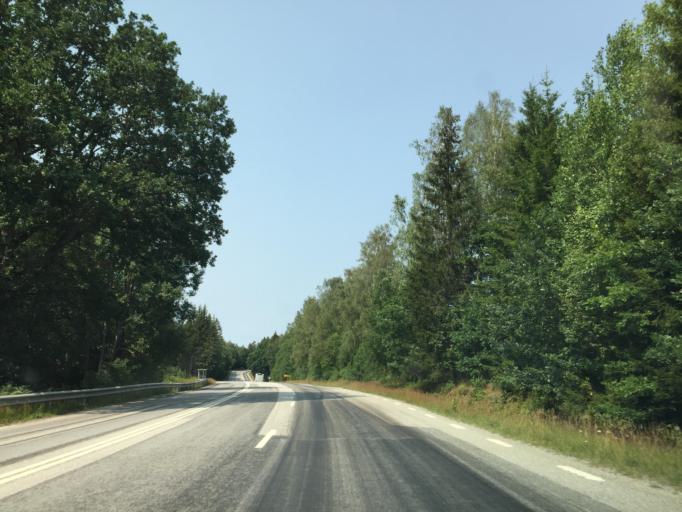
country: SE
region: Vaestra Goetaland
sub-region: Uddevalla Kommun
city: Ljungskile
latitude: 58.1122
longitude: 11.9901
